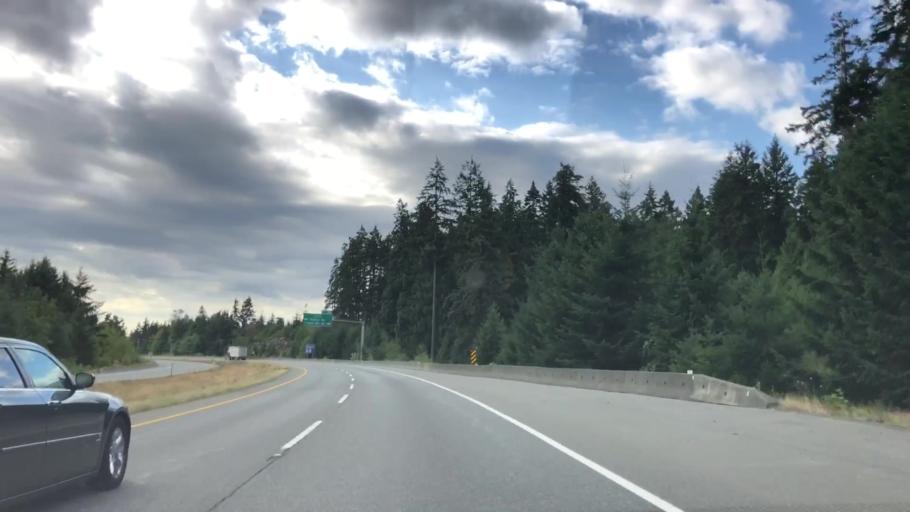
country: CA
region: British Columbia
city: Nanaimo
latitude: 49.2099
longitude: -124.0429
